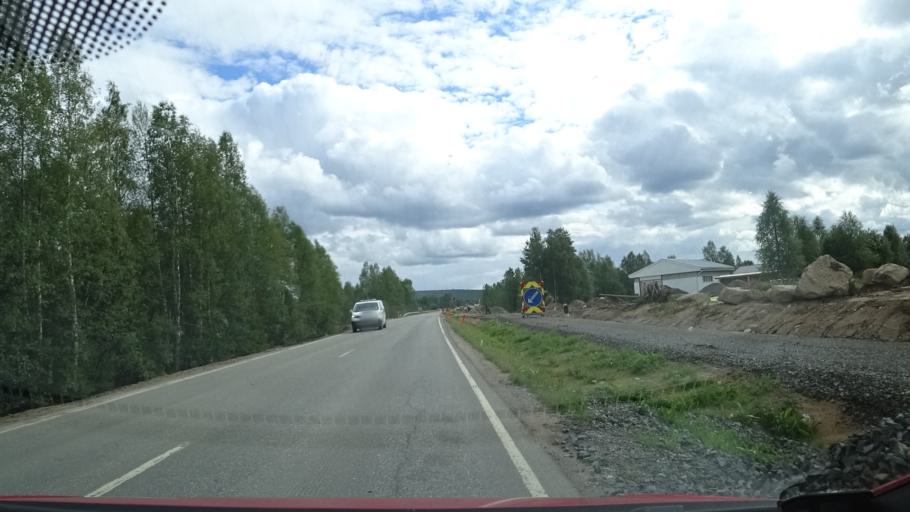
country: FI
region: Lapland
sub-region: Rovaniemi
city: Rovaniemi
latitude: 66.5283
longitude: 25.7402
